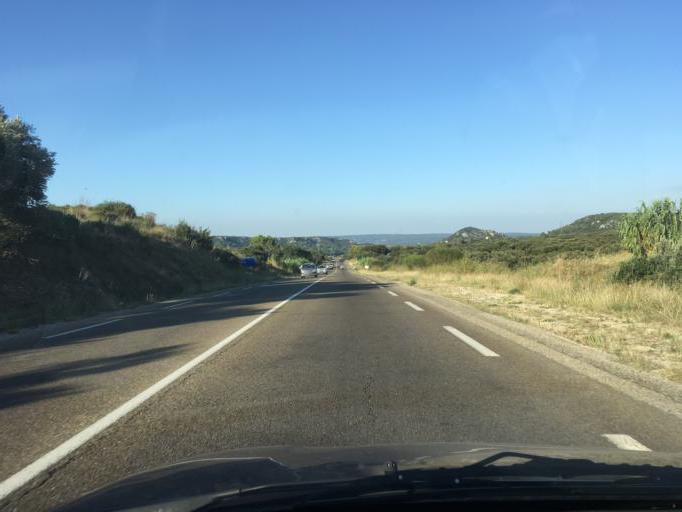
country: FR
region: Languedoc-Roussillon
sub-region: Departement du Gard
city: Ledenon
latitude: 43.9116
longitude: 4.5257
